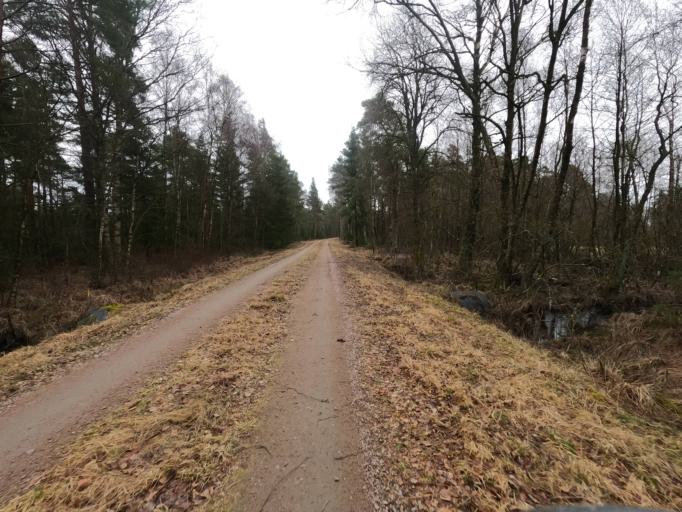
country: SE
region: Kronoberg
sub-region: Markaryds Kommun
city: Stromsnasbruk
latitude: 56.7928
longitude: 13.6227
